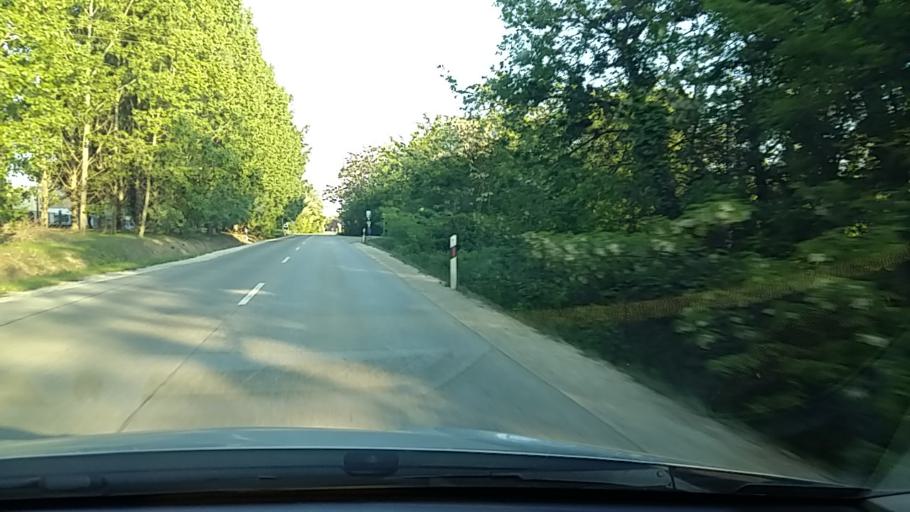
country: HU
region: Pest
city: Orbottyan
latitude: 47.6924
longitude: 19.2540
